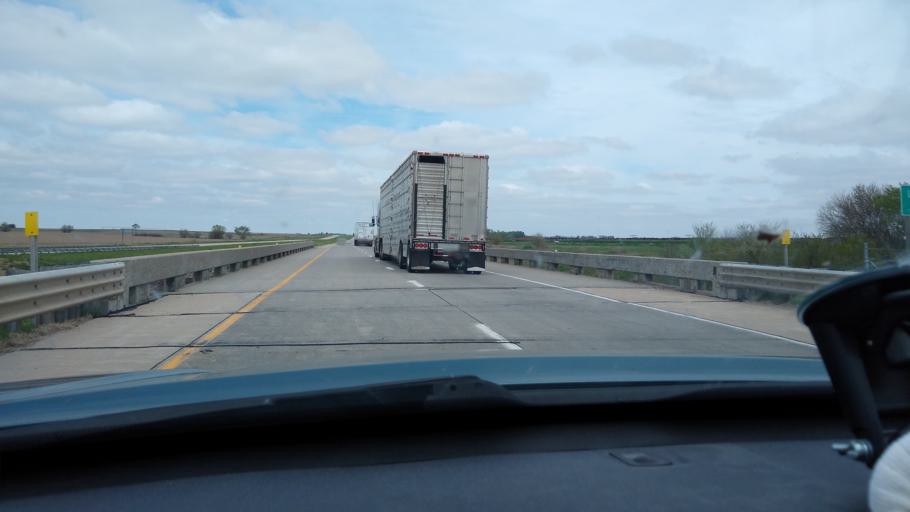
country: US
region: Kansas
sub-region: Ottawa County
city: Minneapolis
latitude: 39.1348
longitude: -97.6687
